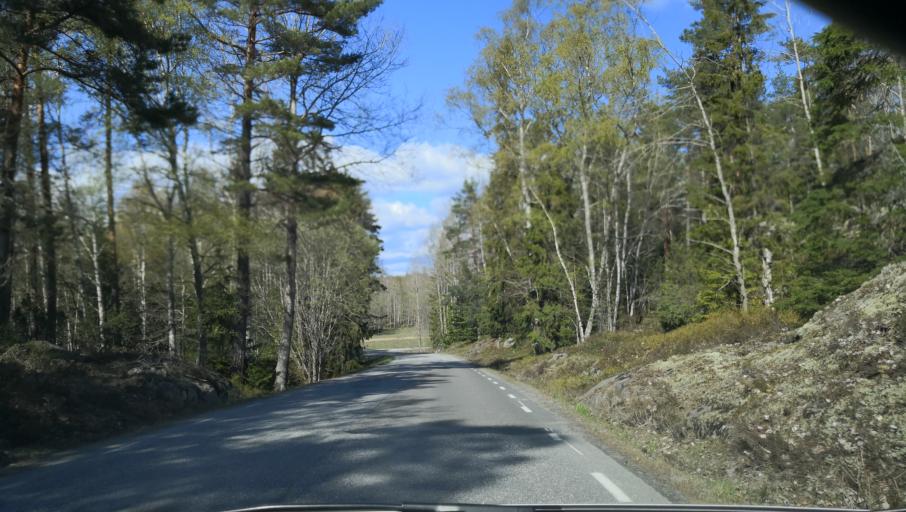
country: SE
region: Stockholm
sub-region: Varmdo Kommun
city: Hemmesta
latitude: 59.3977
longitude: 18.5104
